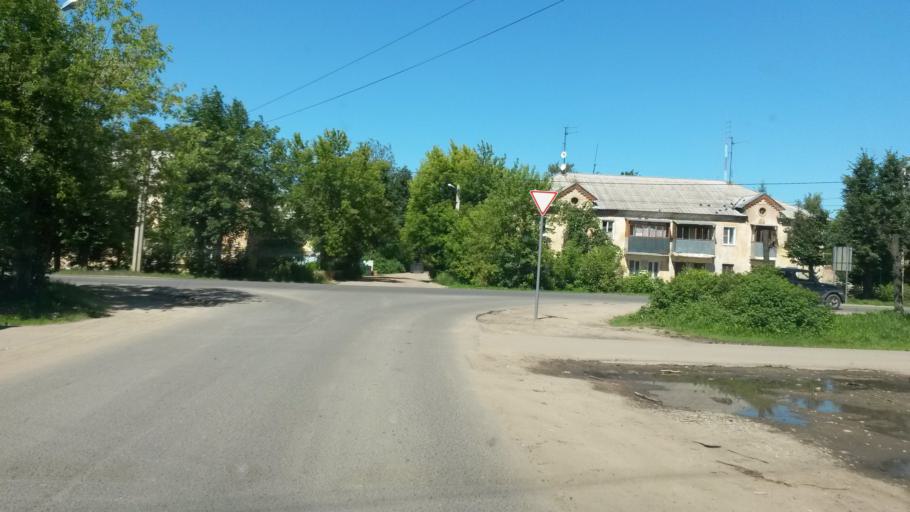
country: RU
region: Ivanovo
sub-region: Gorod Ivanovo
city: Ivanovo
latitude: 56.9822
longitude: 40.9582
